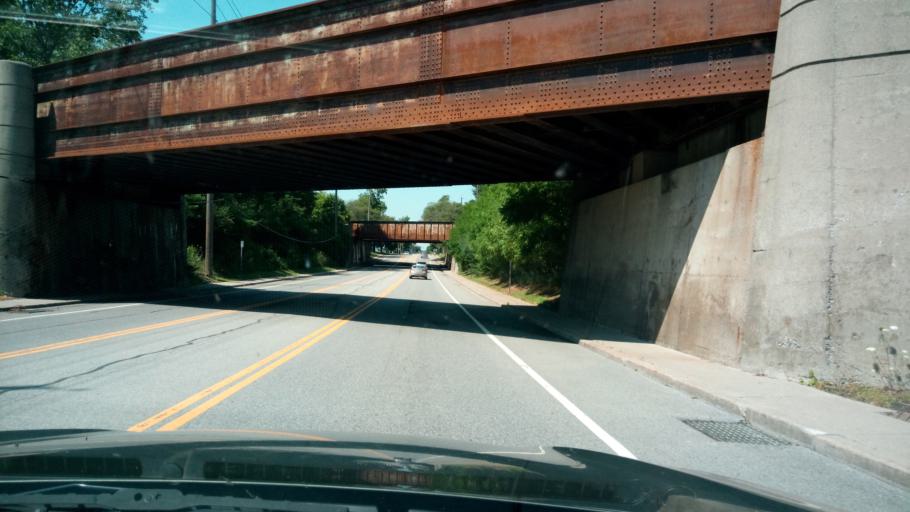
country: US
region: New York
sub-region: Genesee County
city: Batavia
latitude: 42.9846
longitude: -78.1678
